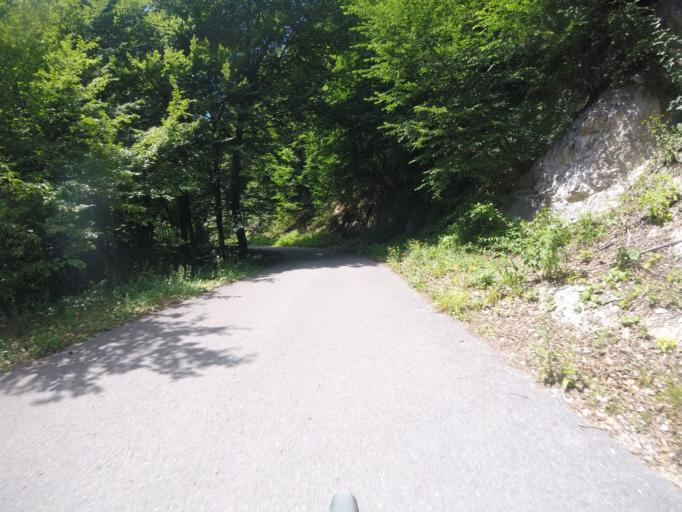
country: SI
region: Kostanjevica na Krki
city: Kostanjevica na Krki
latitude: 45.7687
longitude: 15.4114
